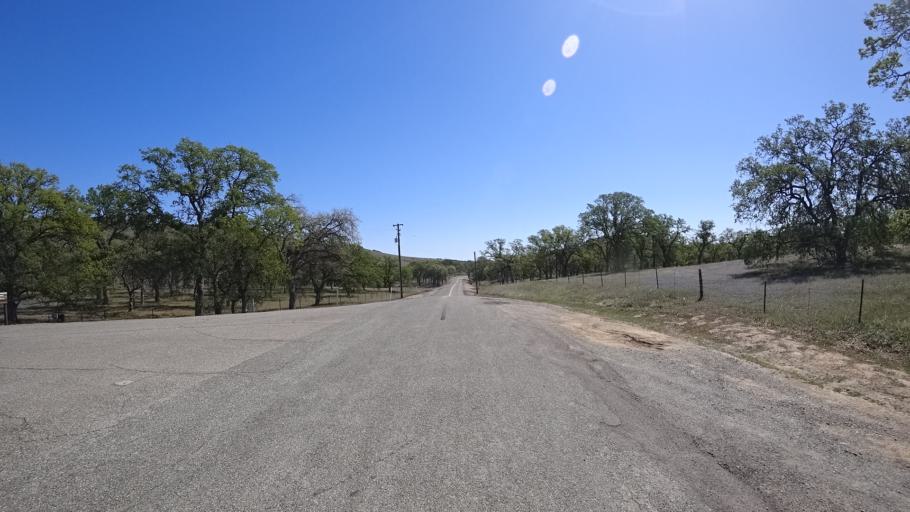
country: US
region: California
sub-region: Glenn County
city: Orland
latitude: 39.7684
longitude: -122.3511
